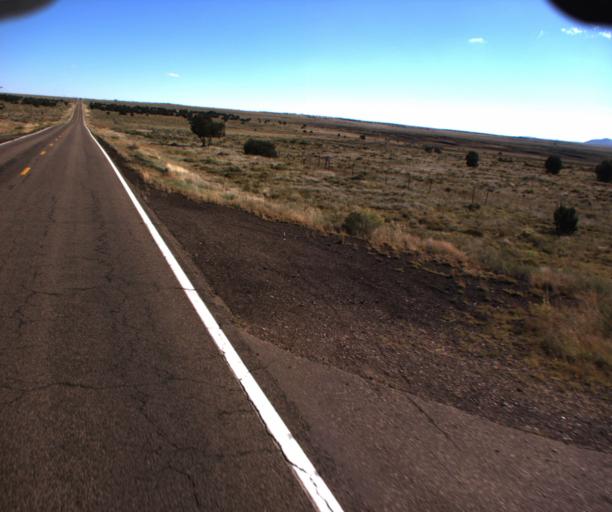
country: US
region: Arizona
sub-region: Navajo County
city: White Mountain Lake
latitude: 34.3445
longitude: -109.7281
